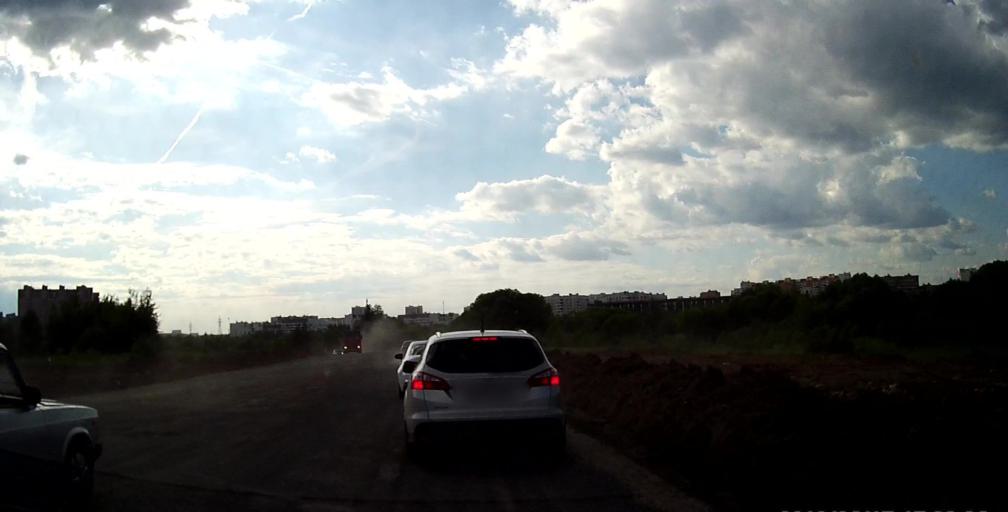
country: RU
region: Moskovskaya
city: Shcherbinka
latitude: 55.5254
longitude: 37.5271
